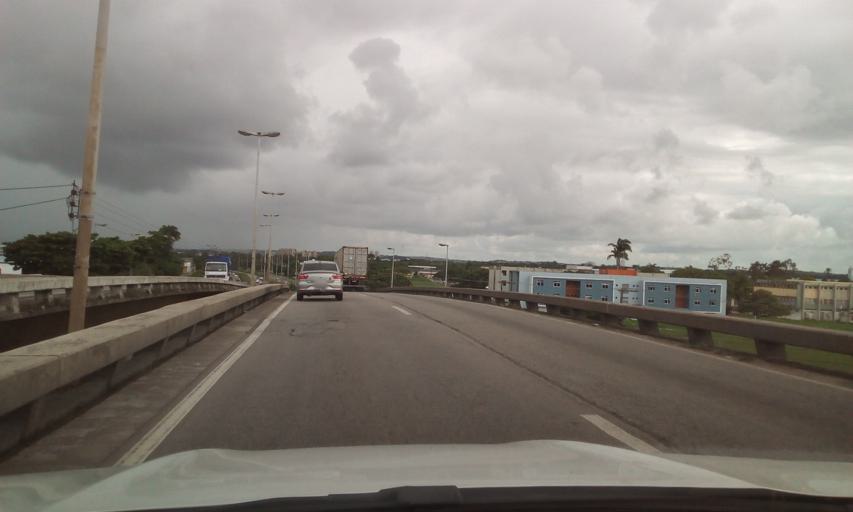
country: BR
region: Pernambuco
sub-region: Recife
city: Recife
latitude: -8.0523
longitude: -34.9462
